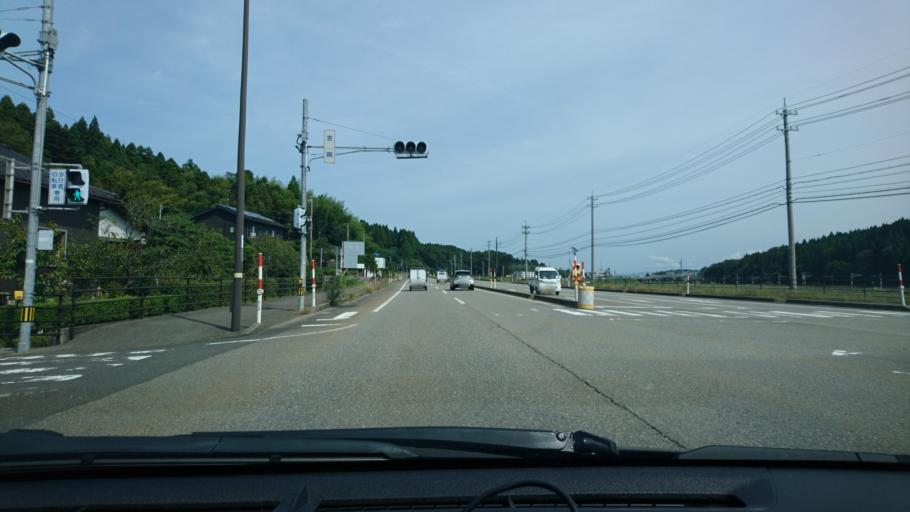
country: JP
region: Fukui
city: Maruoka
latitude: 36.2918
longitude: 136.2992
